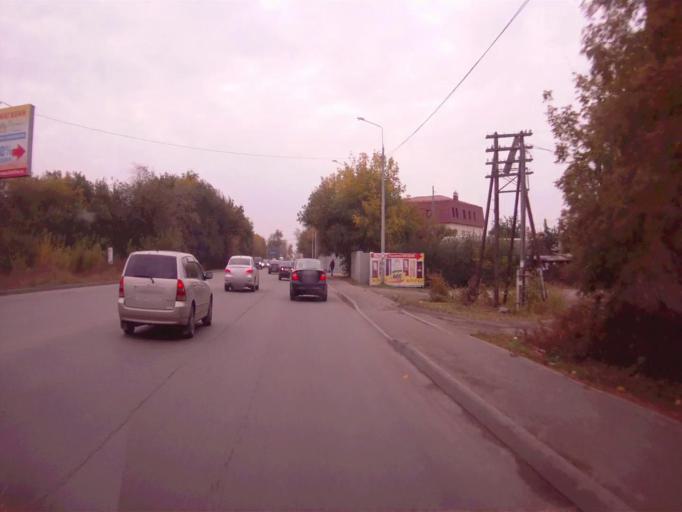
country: RU
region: Chelyabinsk
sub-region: Gorod Chelyabinsk
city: Chelyabinsk
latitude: 55.1301
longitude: 61.3853
